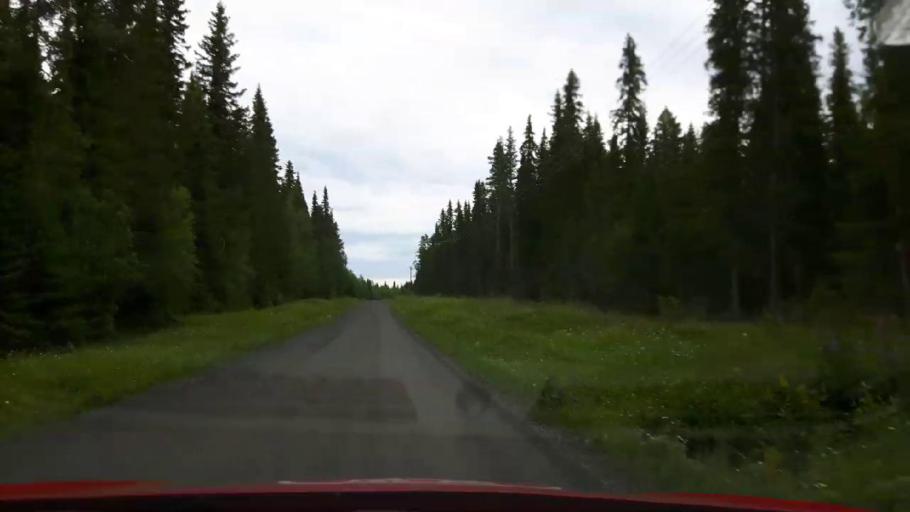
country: SE
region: Jaemtland
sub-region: Stroemsunds Kommun
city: Stroemsund
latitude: 63.4667
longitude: 15.2857
